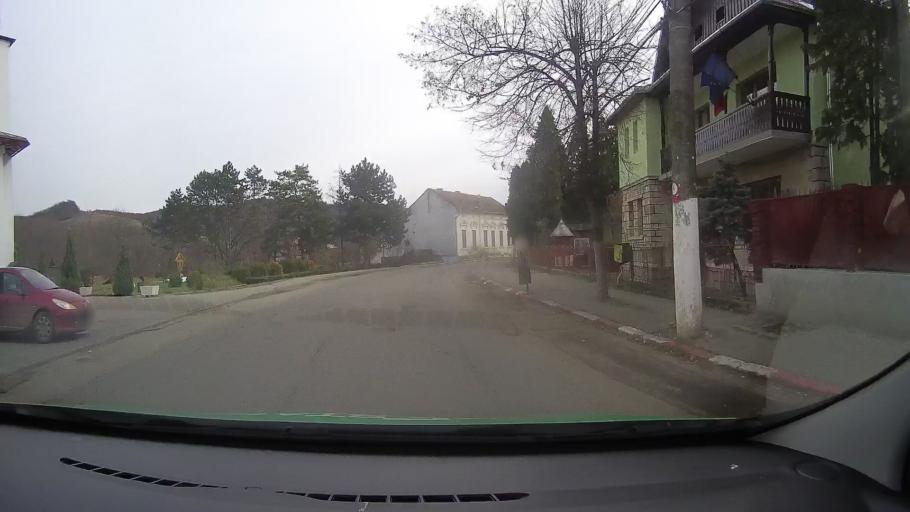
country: RO
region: Hunedoara
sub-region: Comuna Geoagiu
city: Geoagiu
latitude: 45.9247
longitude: 23.1990
